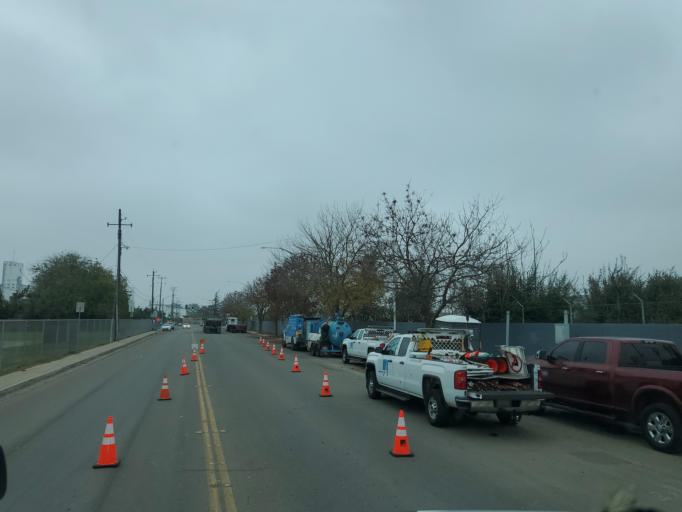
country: US
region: California
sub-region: San Joaquin County
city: Stockton
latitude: 37.9448
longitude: -121.3126
